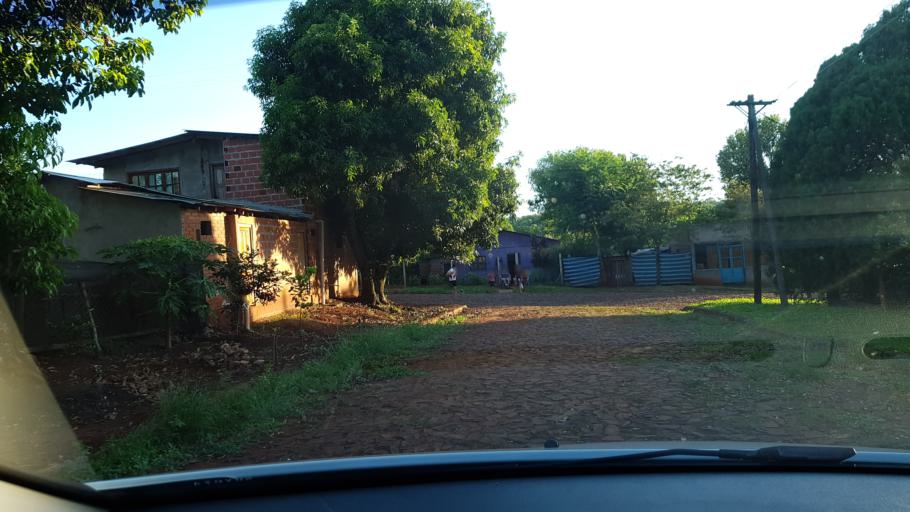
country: AR
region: Misiones
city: Puerto Libertad
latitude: -25.9174
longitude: -54.5816
